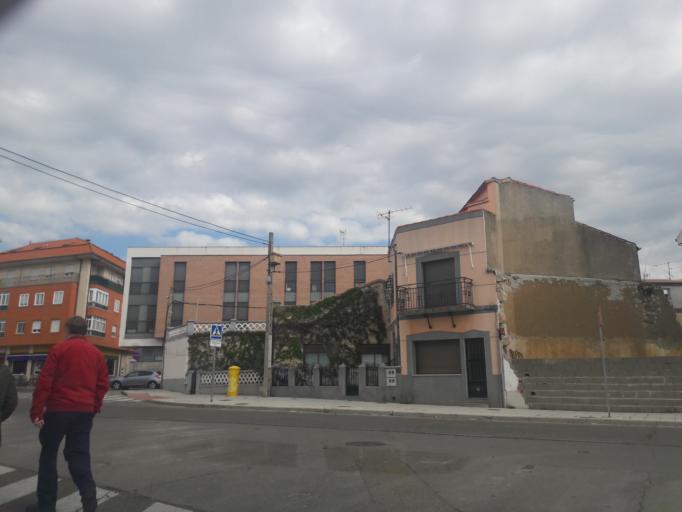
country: ES
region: Castille and Leon
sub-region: Provincia de Salamanca
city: Ciudad Rodrigo
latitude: 40.5967
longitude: -6.5256
